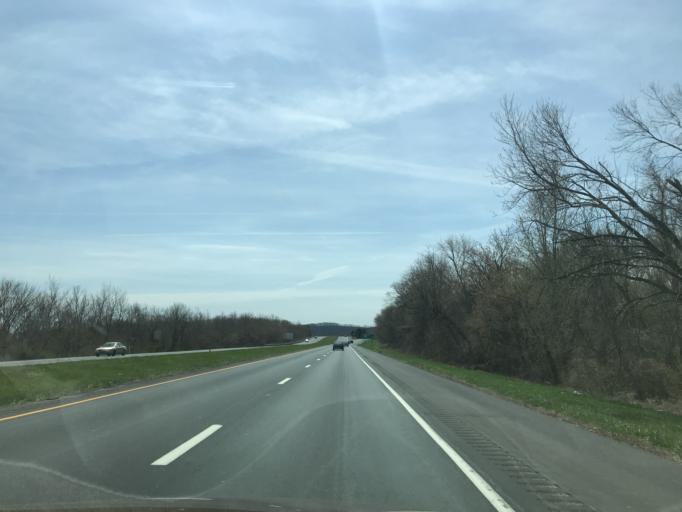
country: US
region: Pennsylvania
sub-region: Snyder County
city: Selinsgrove
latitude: 40.7925
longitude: -76.8609
